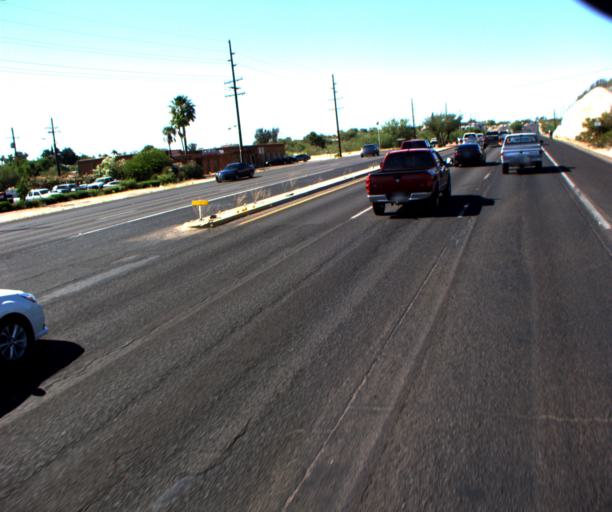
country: US
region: Arizona
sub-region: Pima County
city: Casas Adobes
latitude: 32.3004
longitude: -110.9783
